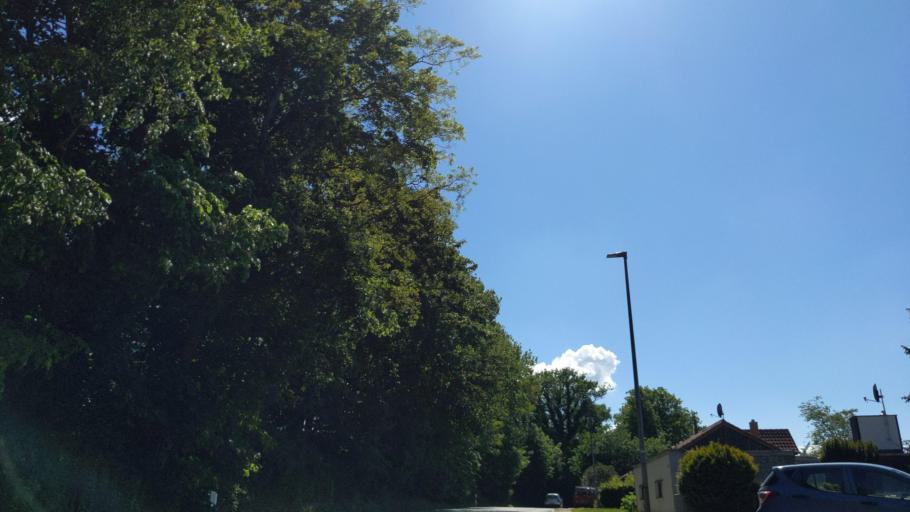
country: DE
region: Schleswig-Holstein
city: Eutin
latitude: 54.1421
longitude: 10.6645
